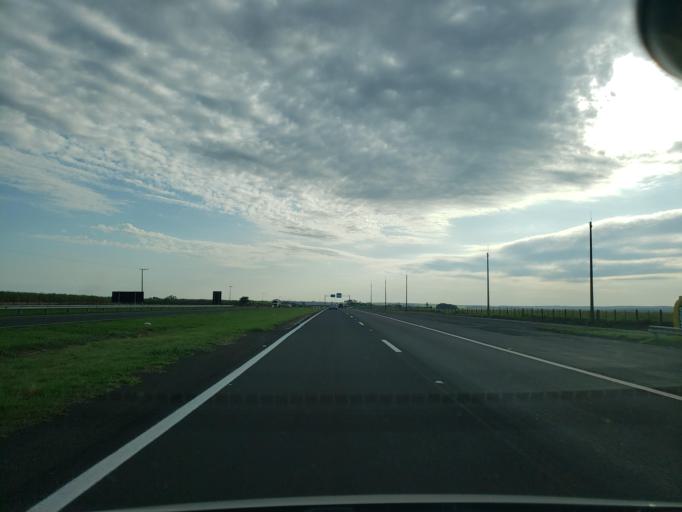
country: BR
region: Sao Paulo
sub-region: Guararapes
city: Guararapes
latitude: -21.2120
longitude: -50.7166
